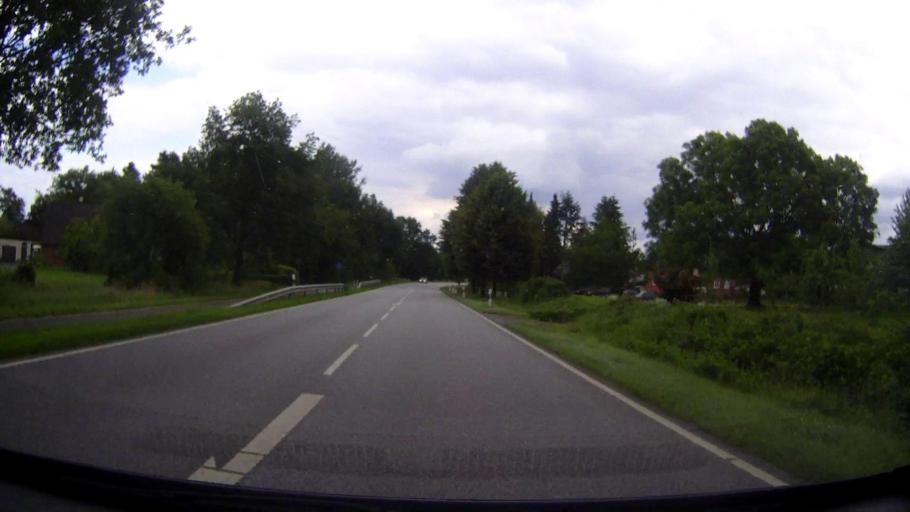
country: DE
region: Schleswig-Holstein
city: Reher
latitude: 54.0671
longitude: 9.5646
